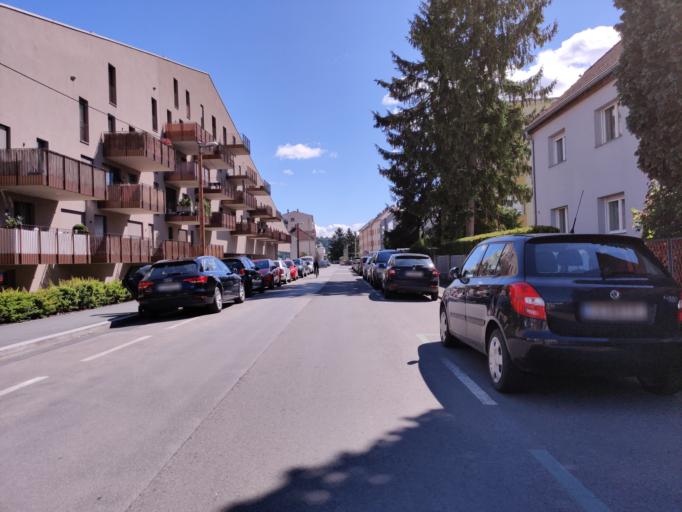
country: AT
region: Styria
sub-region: Graz Stadt
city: Wetzelsdorf
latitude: 47.0719
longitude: 15.4069
